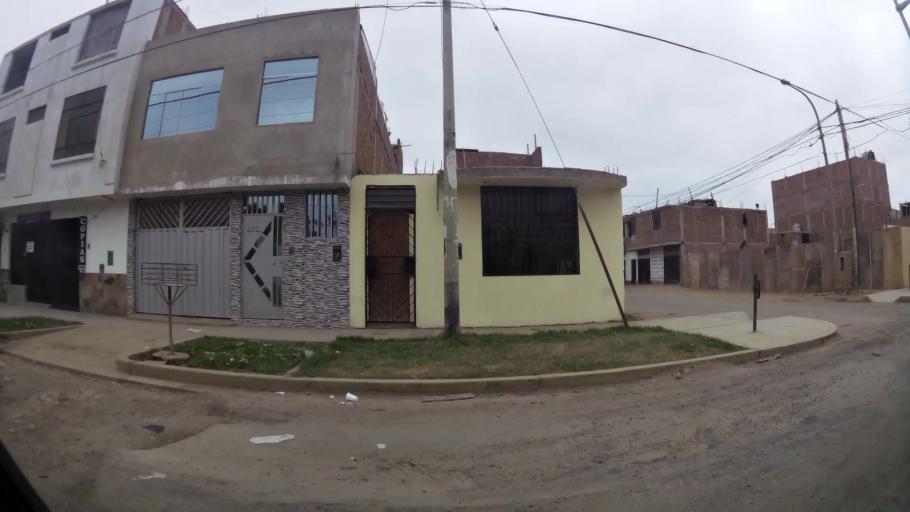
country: PE
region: La Libertad
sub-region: Provincia de Trujillo
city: Buenos Aires
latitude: -8.1222
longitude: -79.0466
